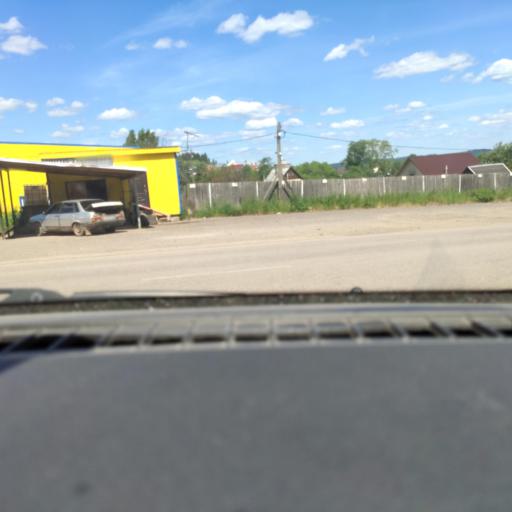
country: RU
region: Perm
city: Chaykovskaya
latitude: 58.1066
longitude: 55.5750
